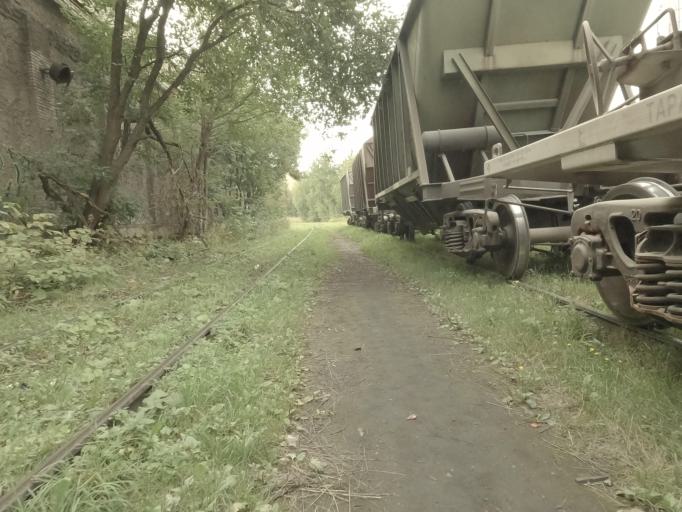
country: RU
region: St.-Petersburg
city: Admiralteisky
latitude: 59.9039
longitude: 30.2831
